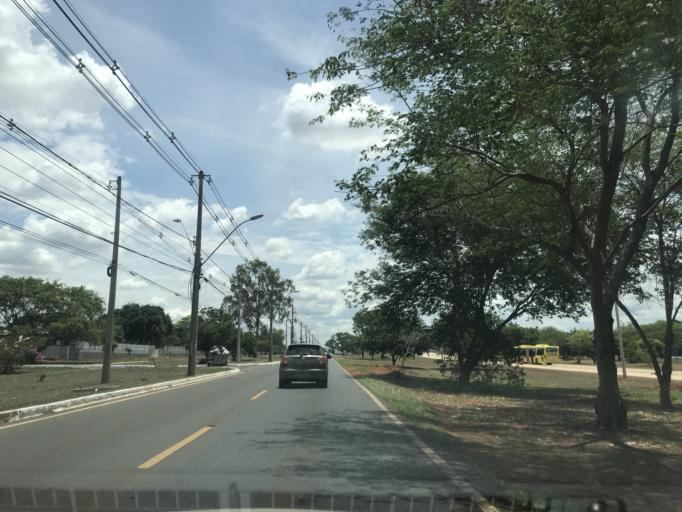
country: BR
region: Federal District
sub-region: Brasilia
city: Brasilia
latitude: -15.8691
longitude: -47.9448
